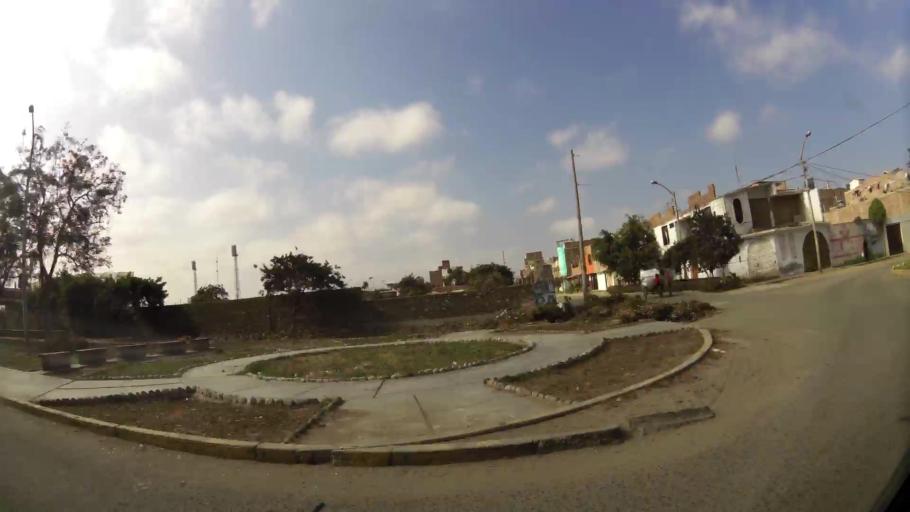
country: PE
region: La Libertad
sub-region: Provincia de Trujillo
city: Trujillo
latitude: -8.1208
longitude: -79.0156
